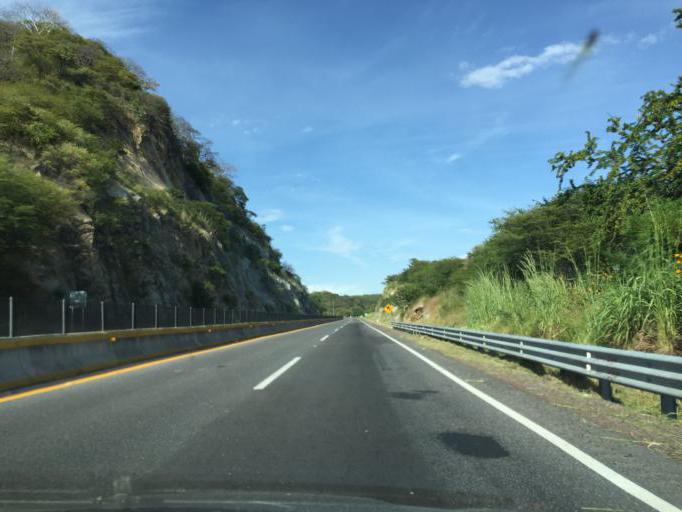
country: MX
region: Morelos
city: Tilzapotla
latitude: 18.3762
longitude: -99.1779
